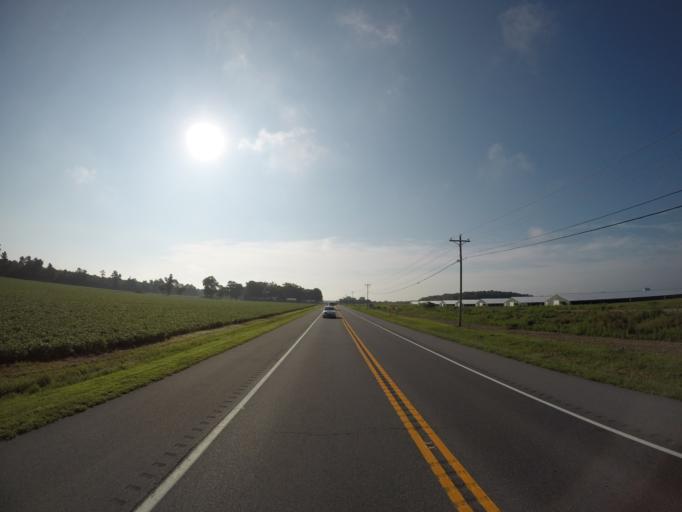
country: US
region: Delaware
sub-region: Sussex County
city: Bridgeville
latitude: 38.7030
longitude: -75.5074
